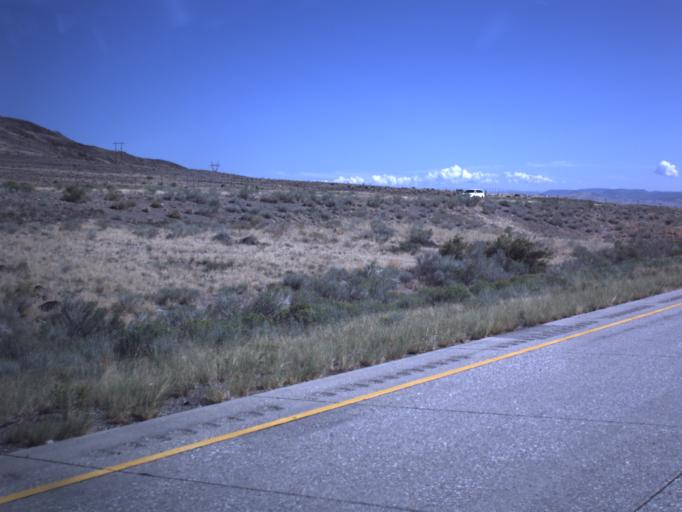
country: US
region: Utah
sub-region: Sevier County
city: Monroe
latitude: 38.6585
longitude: -112.1861
